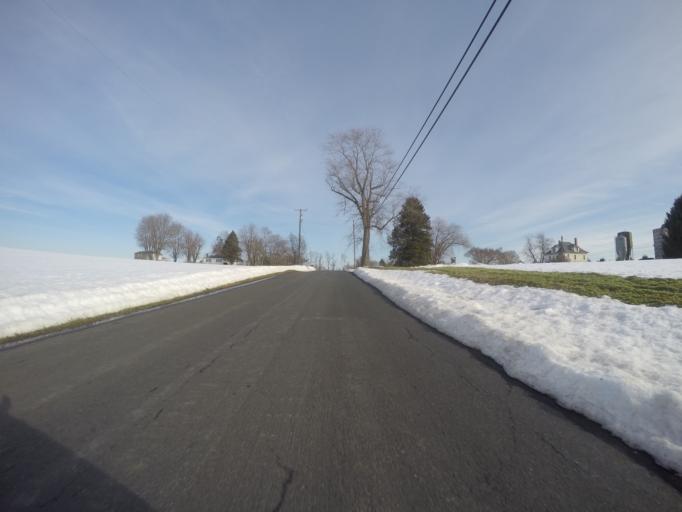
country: US
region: Maryland
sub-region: Baltimore County
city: Hunt Valley
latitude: 39.5530
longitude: -76.5895
